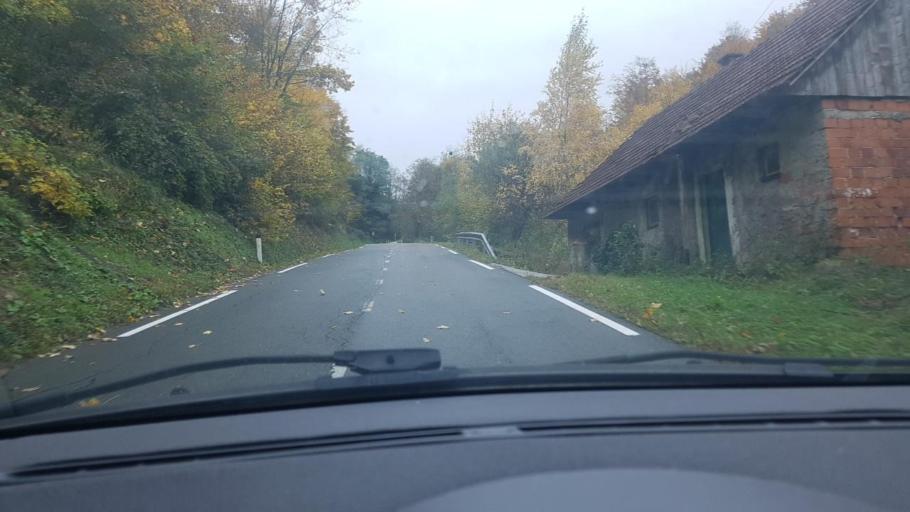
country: SI
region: Rogatec
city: Rogatec
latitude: 46.2690
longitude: 15.7128
